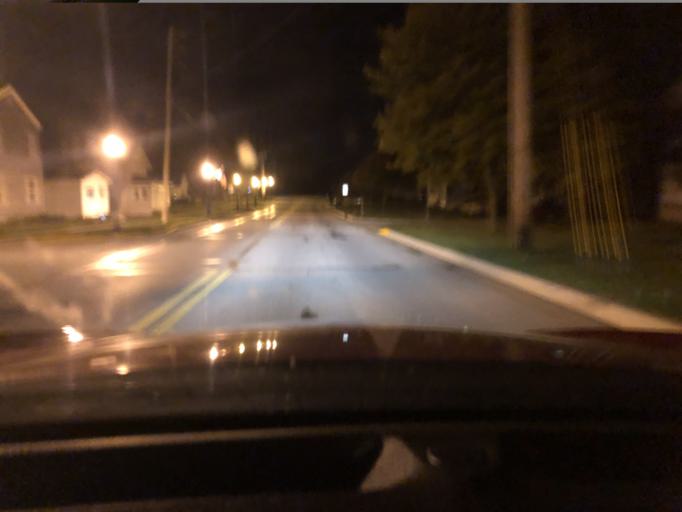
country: US
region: Indiana
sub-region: DeKalb County
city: Waterloo
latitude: 41.4280
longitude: -85.0199
